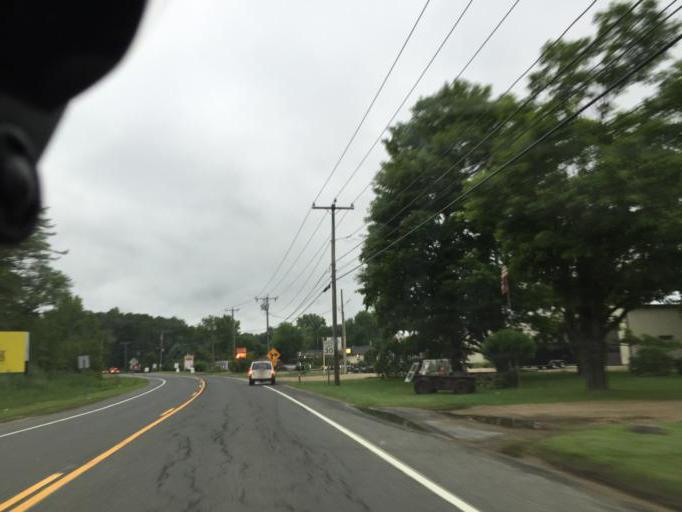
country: US
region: Connecticut
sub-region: Litchfield County
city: Canaan
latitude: 42.0393
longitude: -73.3258
